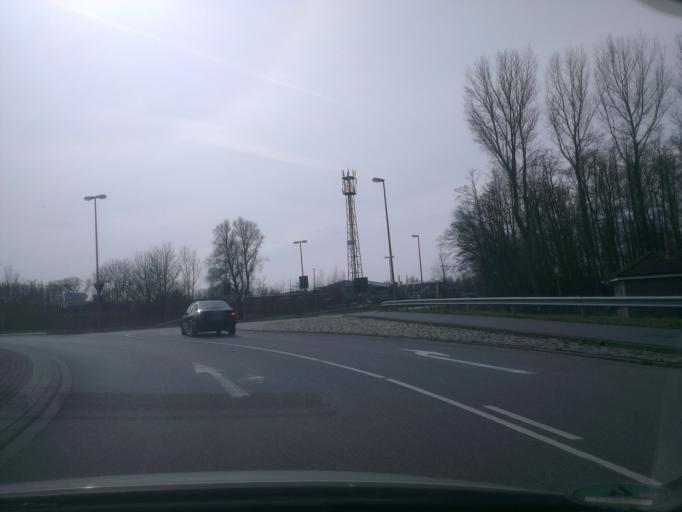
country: DE
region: Lower Saxony
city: Emden
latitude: 53.3576
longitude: 7.1745
